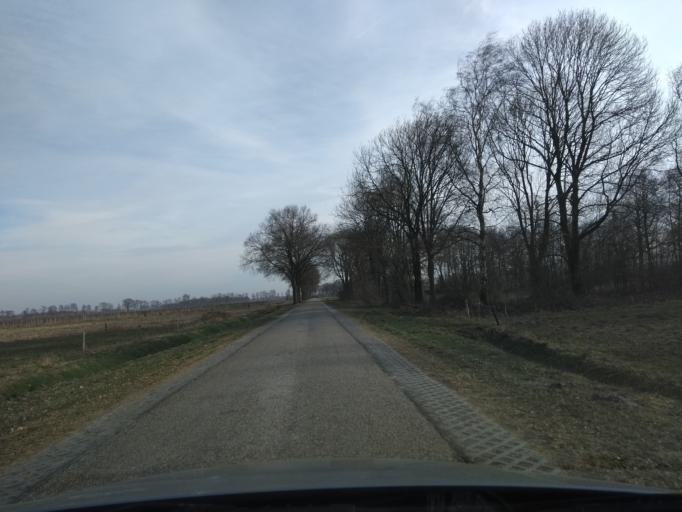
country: NL
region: Overijssel
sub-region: Gemeente Twenterand
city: Vriezenveen
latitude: 52.4117
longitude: 6.6662
